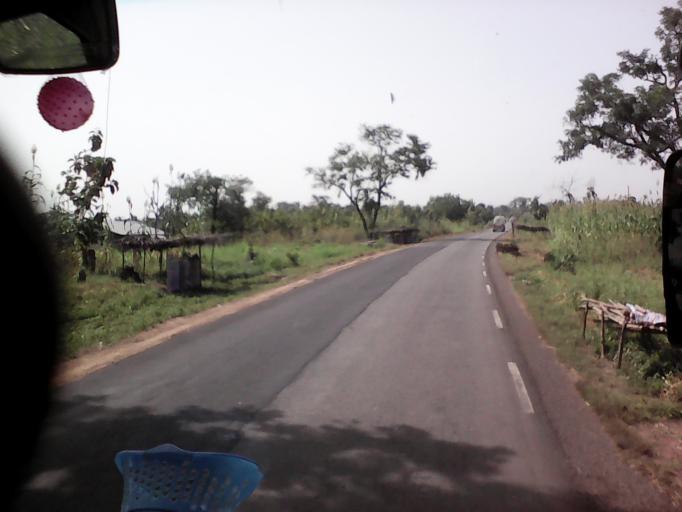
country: TG
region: Centrale
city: Sokode
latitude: 8.7882
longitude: 1.0679
